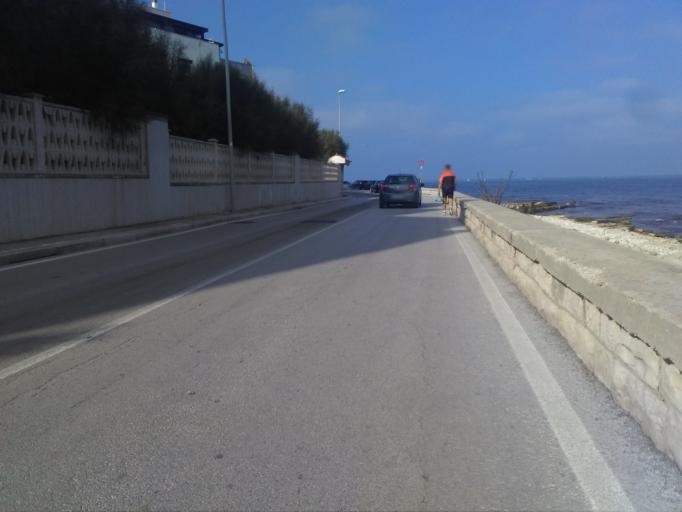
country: IT
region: Apulia
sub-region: Provincia di Bari
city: San Paolo
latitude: 41.1620
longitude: 16.7617
